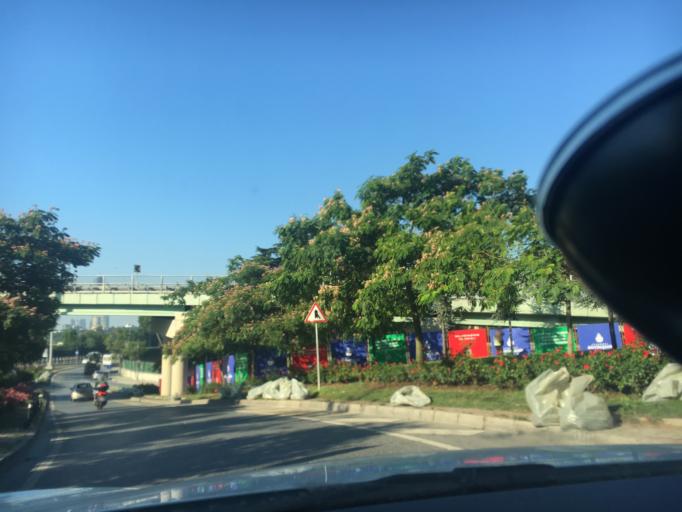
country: TR
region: Istanbul
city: Sisli
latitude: 41.1077
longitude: 29.0140
